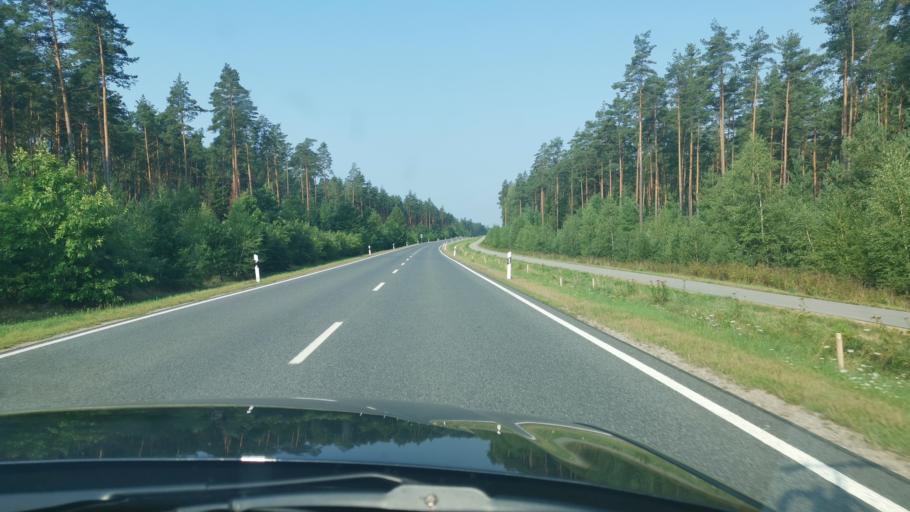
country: DE
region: Bavaria
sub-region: Upper Palatinate
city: Wernberg-Koblitz
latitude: 49.5400
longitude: 12.0985
